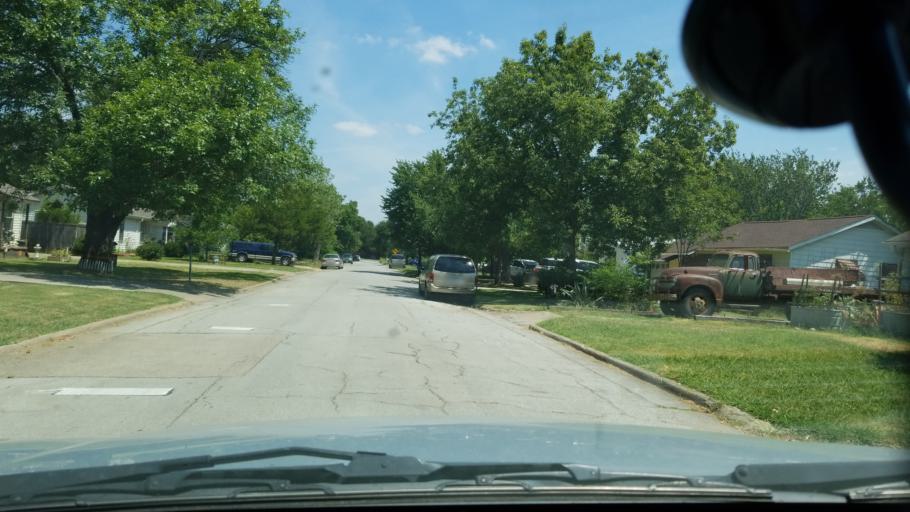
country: US
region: Texas
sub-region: Dallas County
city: Grand Prairie
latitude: 32.7539
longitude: -96.9543
